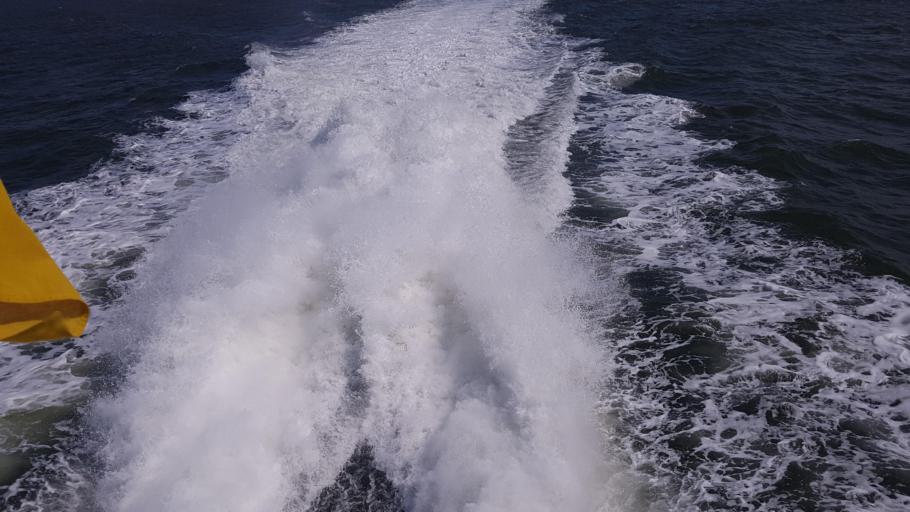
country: DE
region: Schleswig-Holstein
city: Pellworm
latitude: 54.4855
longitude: 8.7424
